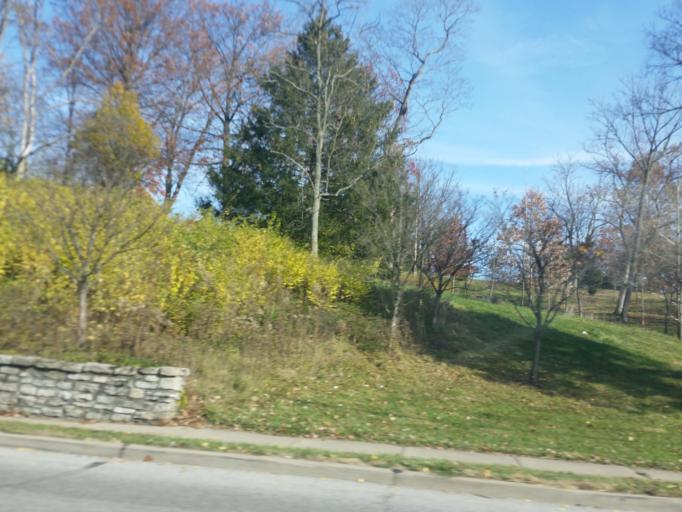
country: US
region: Ohio
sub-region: Hamilton County
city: Monfort Heights
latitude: 39.1764
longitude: -84.5623
